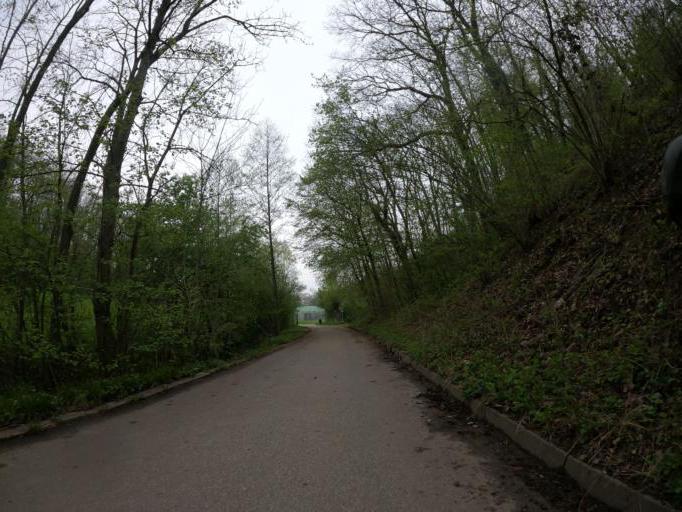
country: DE
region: Baden-Wuerttemberg
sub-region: Regierungsbezirk Stuttgart
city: Markgroningen
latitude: 48.9125
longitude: 9.0870
